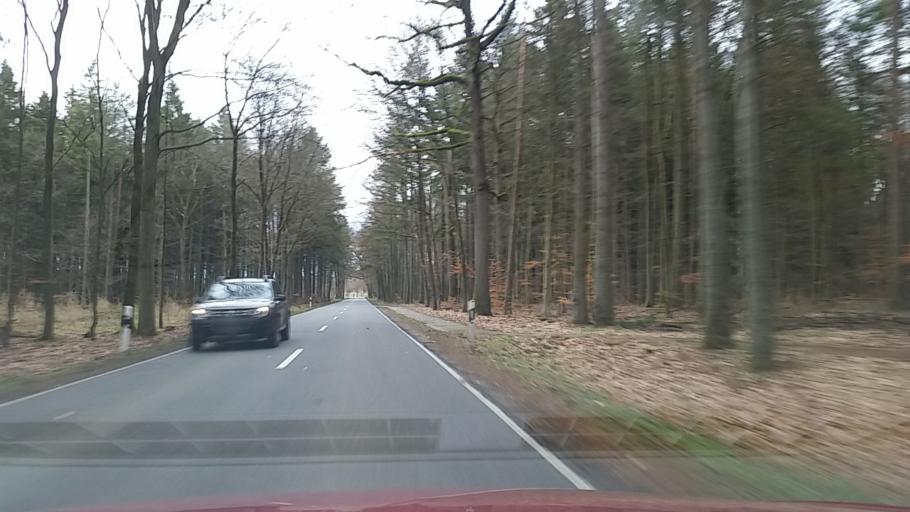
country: DE
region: Lower Saxony
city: Zernien
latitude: 53.1084
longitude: 10.9459
